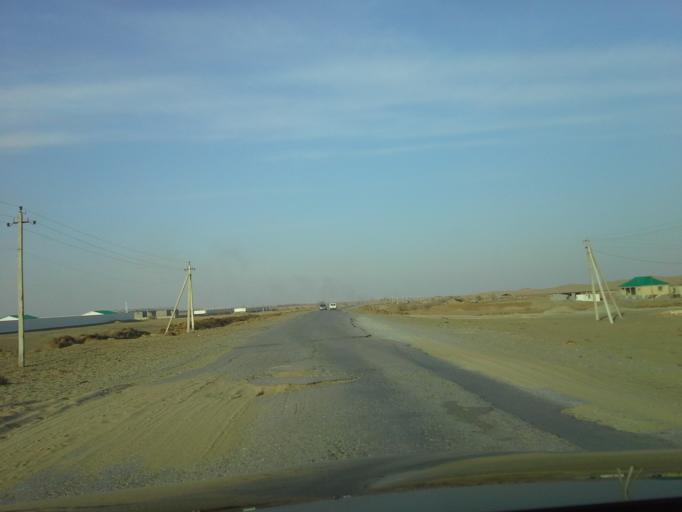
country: TM
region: Ahal
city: Abadan
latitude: 38.1825
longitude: 58.0412
